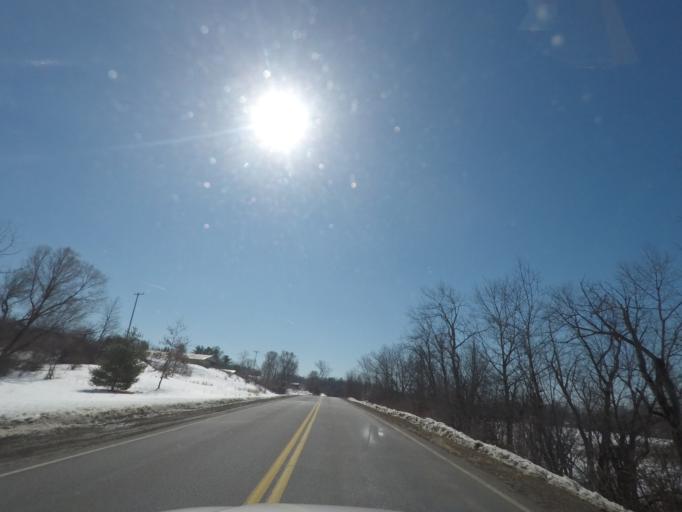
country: US
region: New York
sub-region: Saratoga County
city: Stillwater
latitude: 42.9896
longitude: -73.6033
